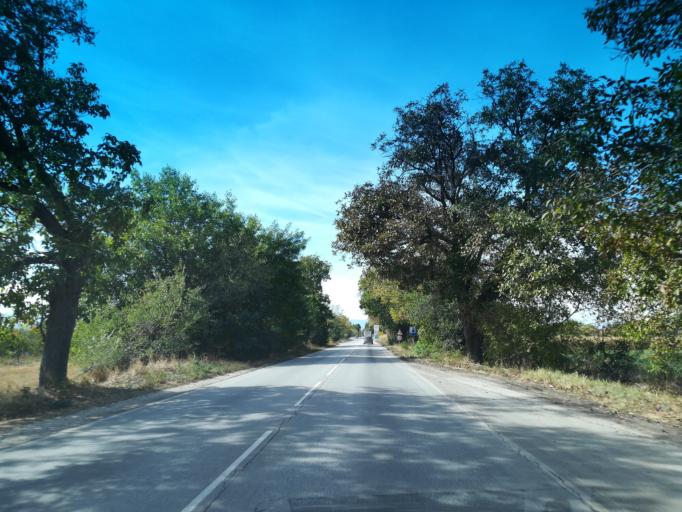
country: BG
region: Plovdiv
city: Stamboliyski
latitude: 42.1343
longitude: 24.6162
